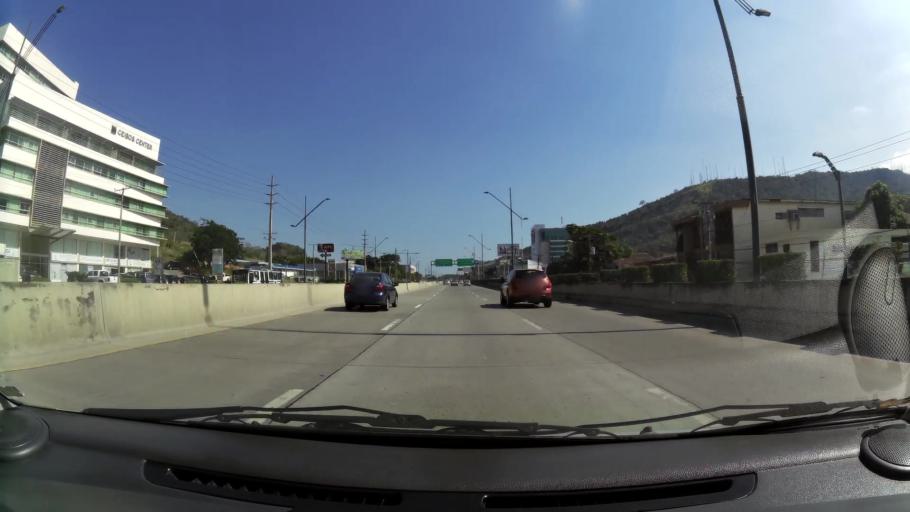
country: EC
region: Guayas
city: Guayaquil
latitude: -2.1692
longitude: -79.9373
